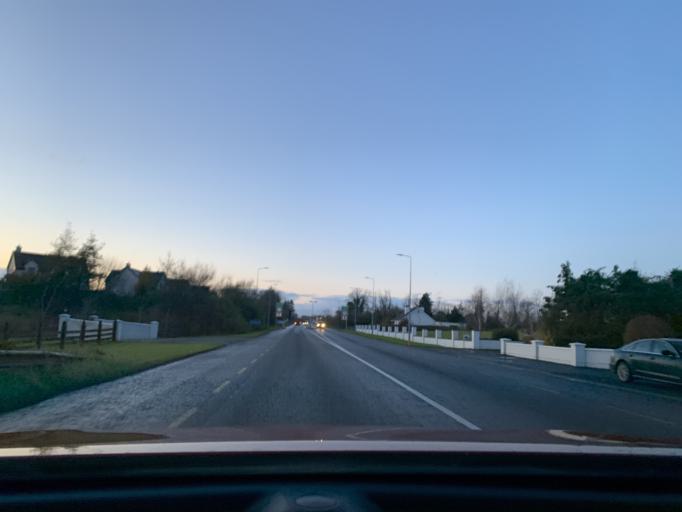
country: IE
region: Connaught
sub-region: County Leitrim
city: Carrick-on-Shannon
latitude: 53.9416
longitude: -8.0665
